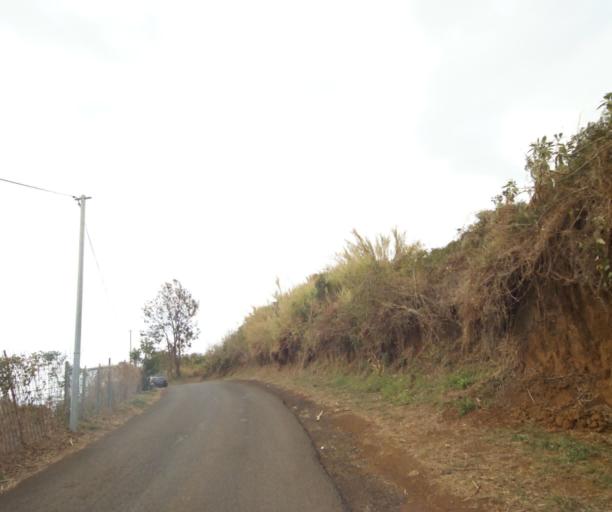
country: RE
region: Reunion
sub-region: Reunion
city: Saint-Paul
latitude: -21.0286
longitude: 55.3014
